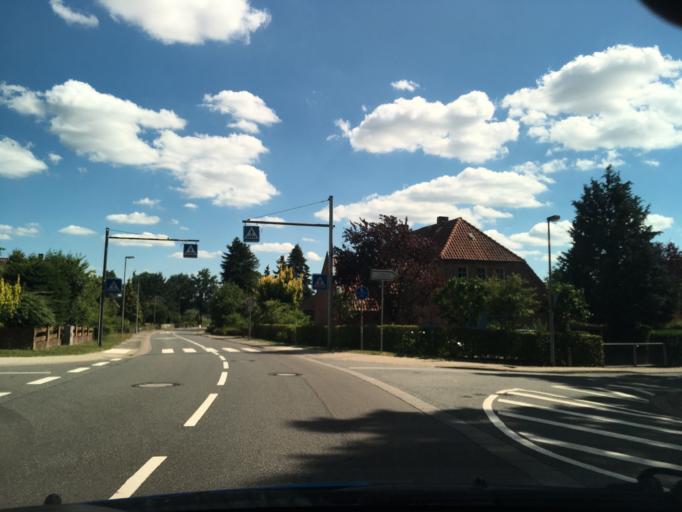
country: DE
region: Lower Saxony
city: Celle
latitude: 52.6319
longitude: 10.1158
